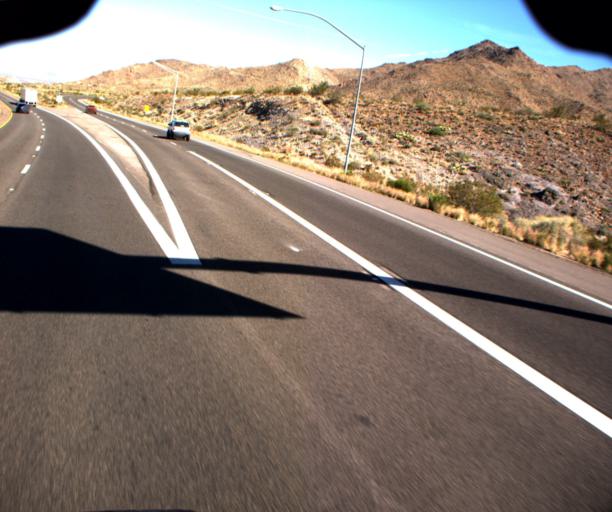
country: US
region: Arizona
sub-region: Mohave County
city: Kingman
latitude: 35.2171
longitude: -114.1170
